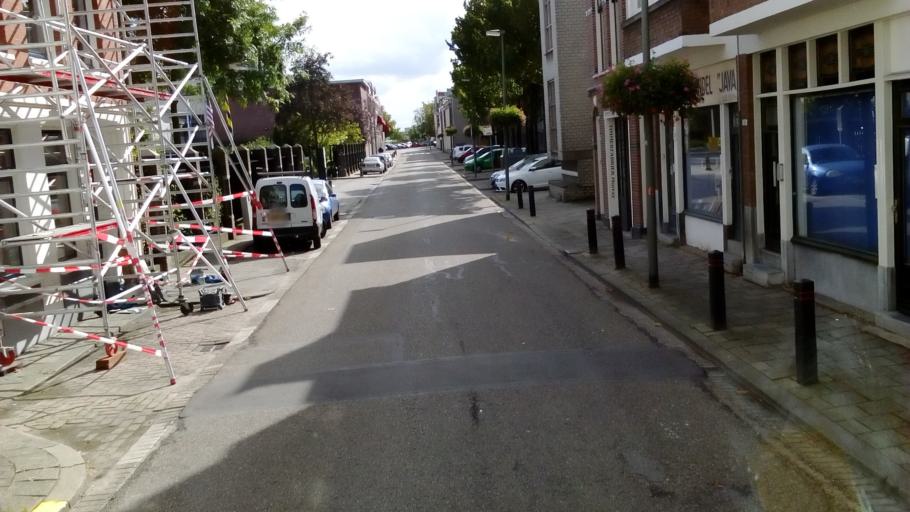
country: NL
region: South Holland
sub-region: Gemeente Schiedam
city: Schiedam
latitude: 51.9088
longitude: 4.4064
